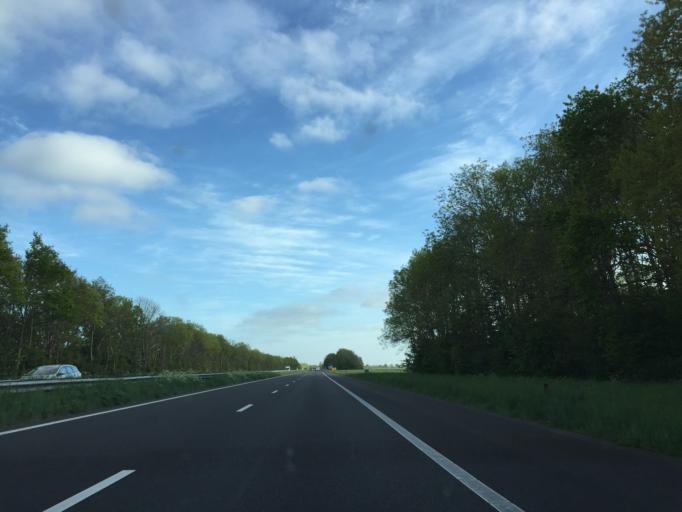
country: NL
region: North Holland
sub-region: Gemeente Hollands Kroon
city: Den Oever
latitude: 52.8674
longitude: 5.0221
